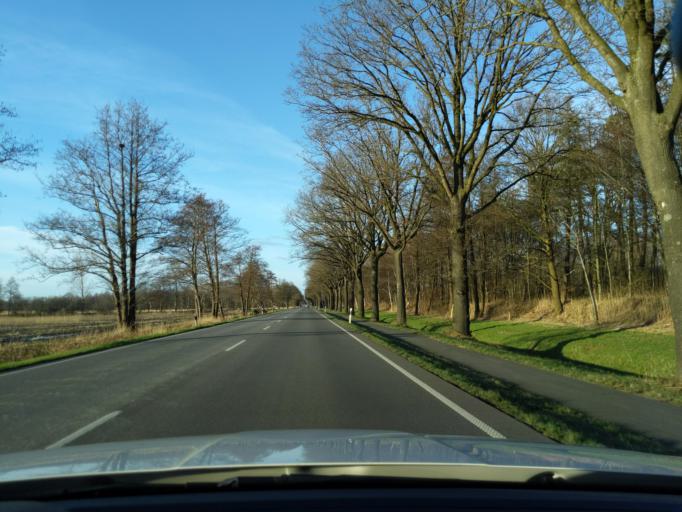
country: DE
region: Lower Saxony
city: Geeste
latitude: 52.6112
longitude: 7.3069
